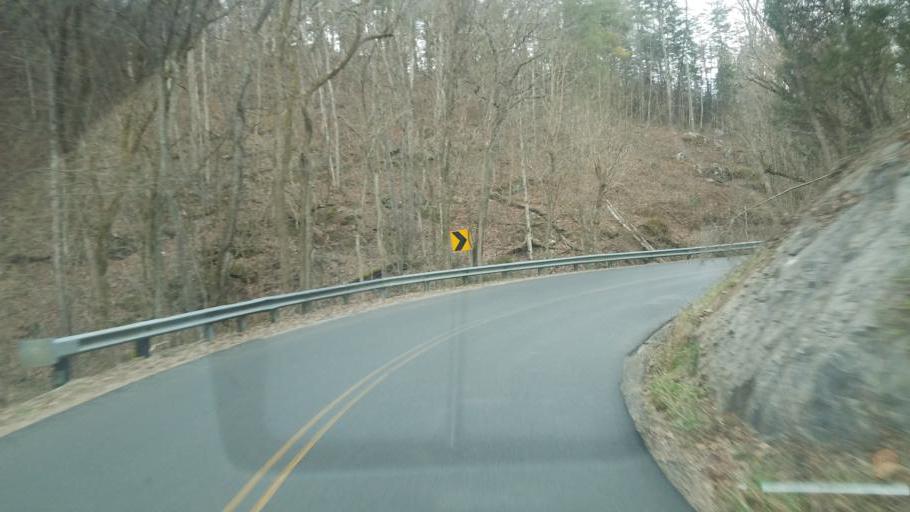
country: US
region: Virginia
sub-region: Giles County
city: Pearisburg
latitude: 37.2440
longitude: -80.6991
